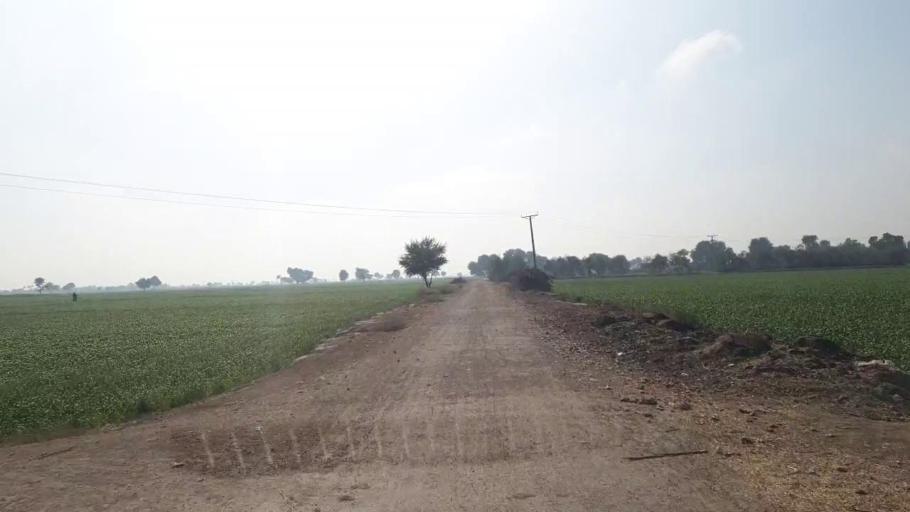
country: PK
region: Sindh
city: Shahdadpur
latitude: 26.0223
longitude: 68.5744
